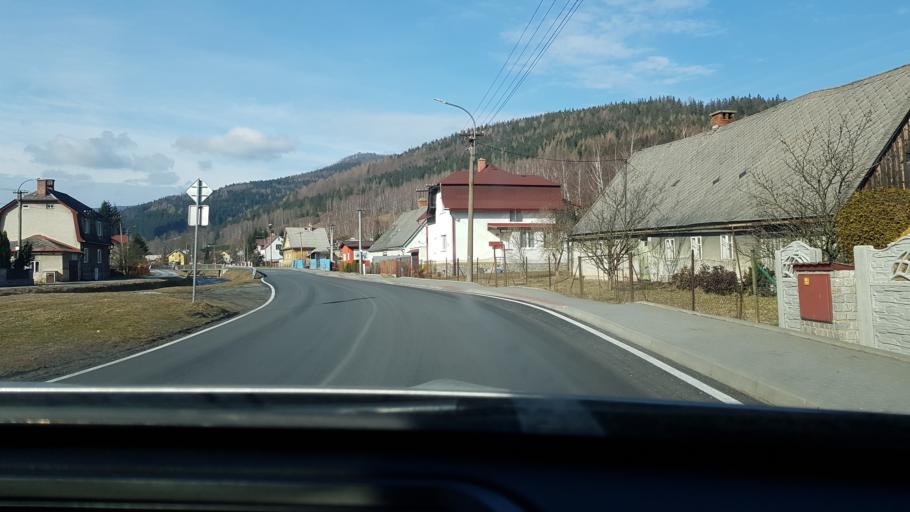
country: CZ
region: Olomoucky
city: Vapenna
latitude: 50.2264
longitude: 17.1277
